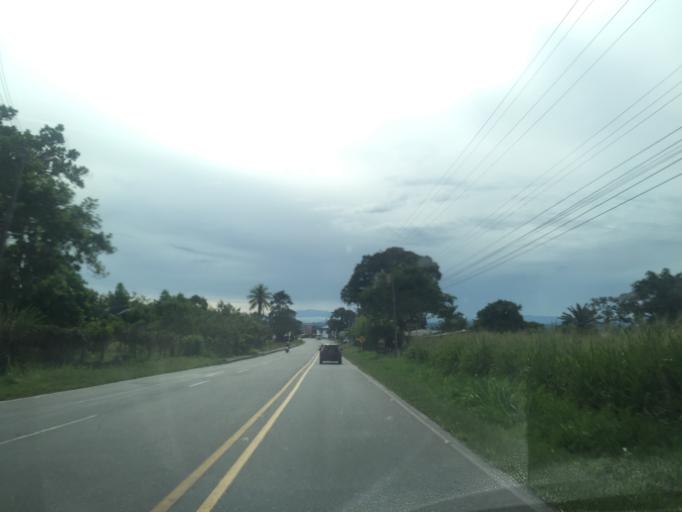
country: CO
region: Quindio
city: Armenia
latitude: 4.4985
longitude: -75.7281
